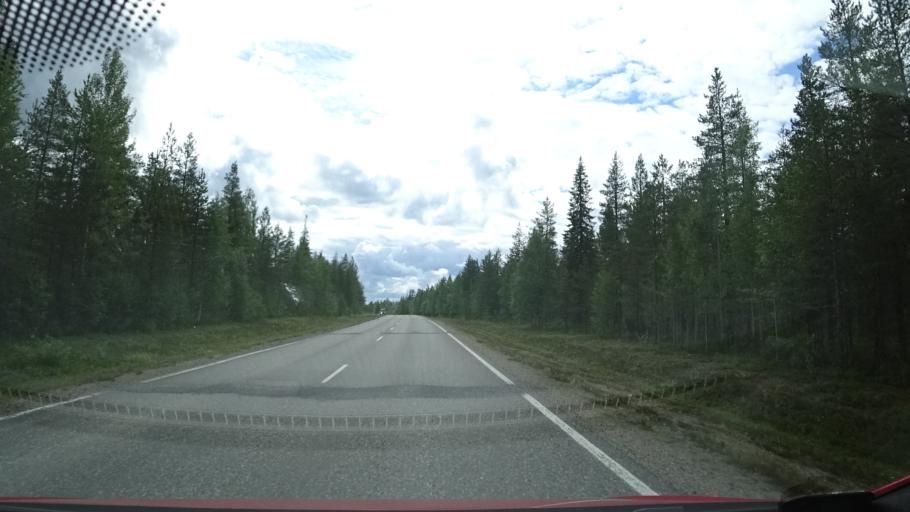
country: FI
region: Lapland
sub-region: Tunturi-Lappi
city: Kittilae
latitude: 67.5125
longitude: 24.9005
